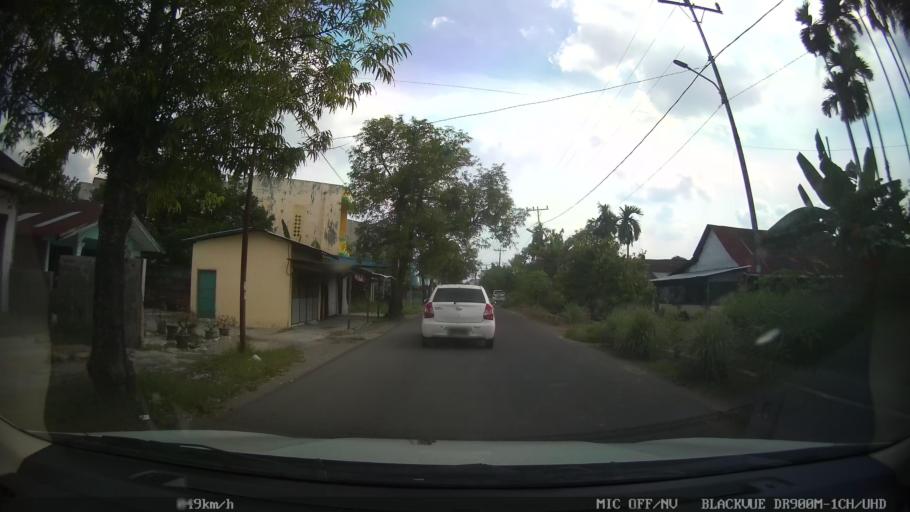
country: ID
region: North Sumatra
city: Binjai
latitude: 3.6219
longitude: 98.5006
